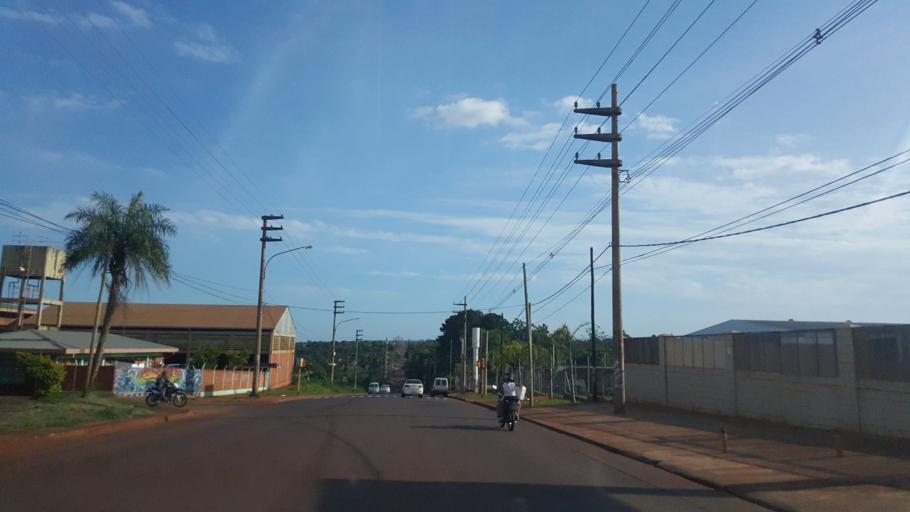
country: AR
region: Misiones
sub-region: Departamento de Capital
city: Posadas
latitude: -27.4157
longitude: -55.9127
